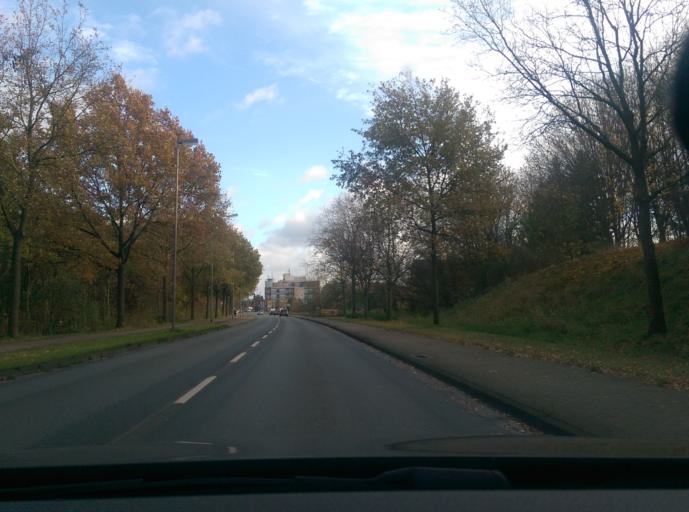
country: DE
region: Lower Saxony
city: Celle
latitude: 52.6338
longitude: 10.0747
